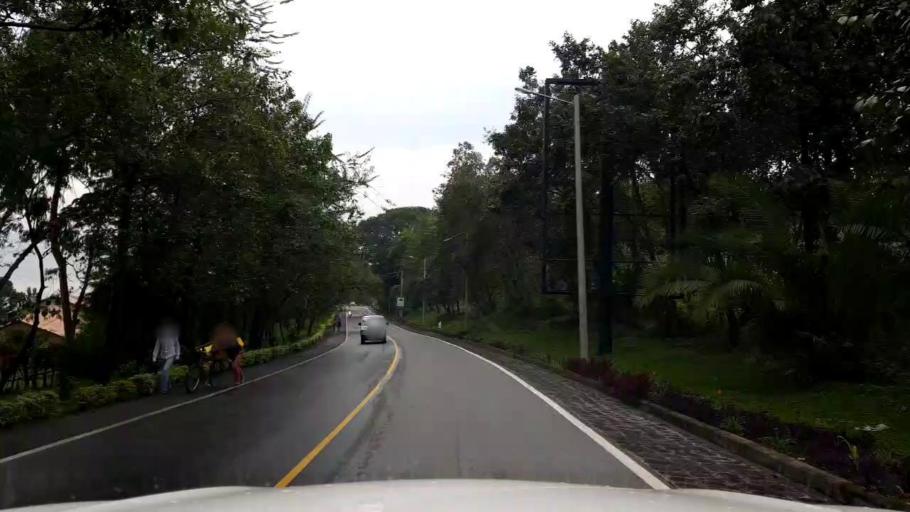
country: RW
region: Western Province
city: Gisenyi
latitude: -1.7042
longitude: 29.2693
